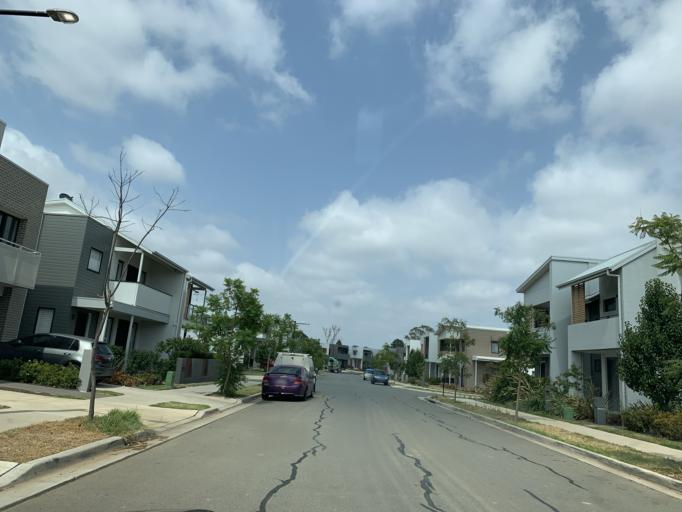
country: AU
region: New South Wales
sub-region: Blacktown
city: Blacktown
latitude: -33.7582
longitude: 150.9029
